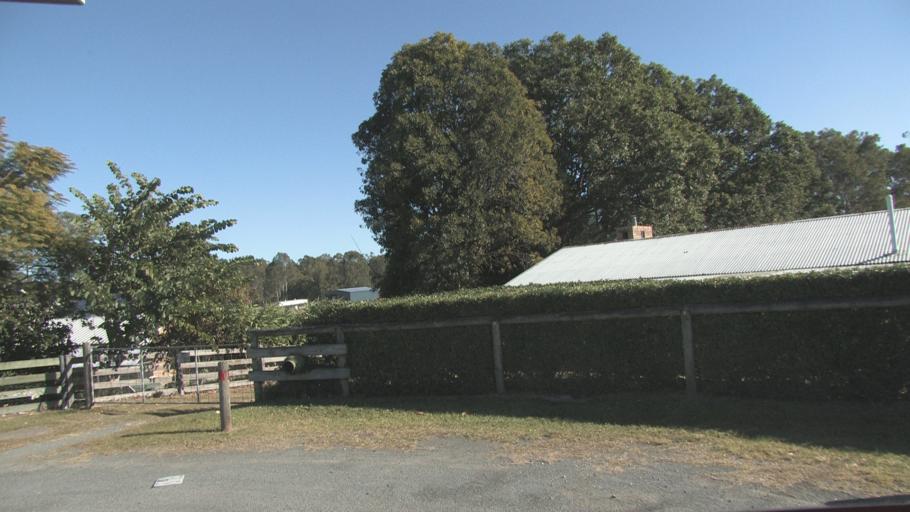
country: AU
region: Queensland
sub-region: Logan
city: North Maclean
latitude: -27.7821
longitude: 153.0025
